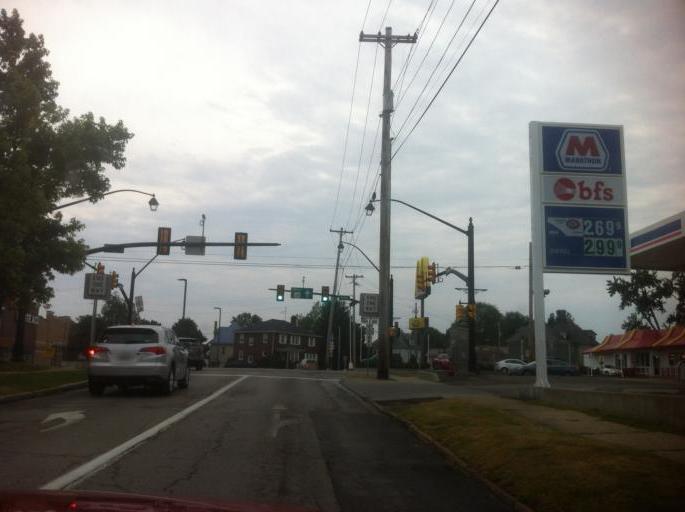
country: US
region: Pennsylvania
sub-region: Mercer County
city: Grove City
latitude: 41.1587
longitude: -80.0879
